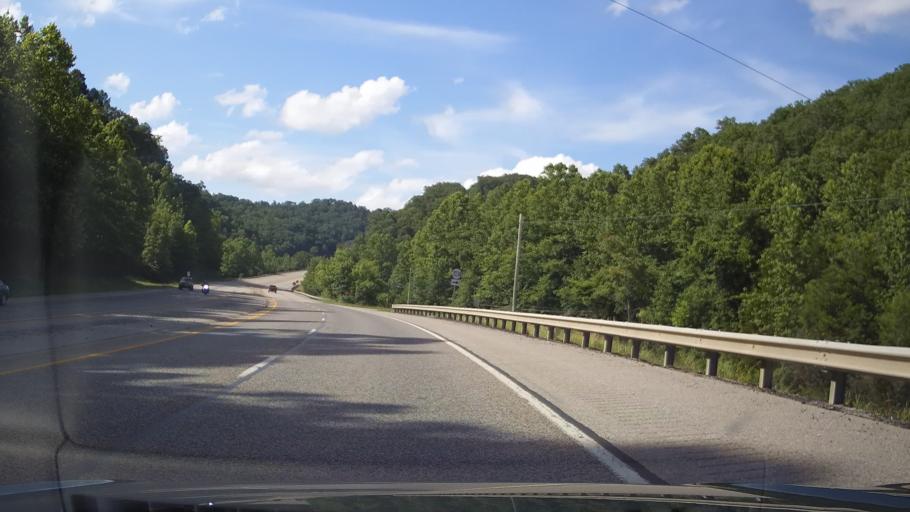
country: US
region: Kentucky
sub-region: Lawrence County
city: Louisa
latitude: 38.0229
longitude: -82.6514
